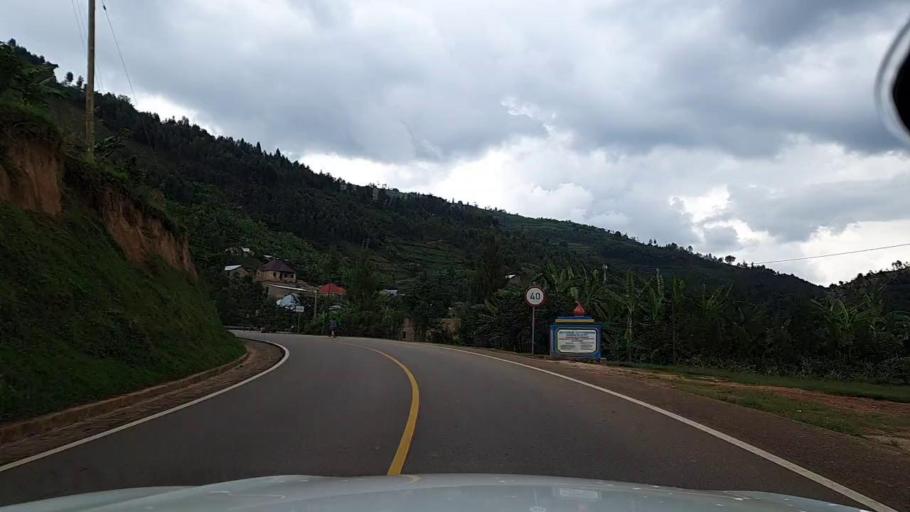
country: RW
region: Northern Province
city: Byumba
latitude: -1.6758
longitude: 30.0950
